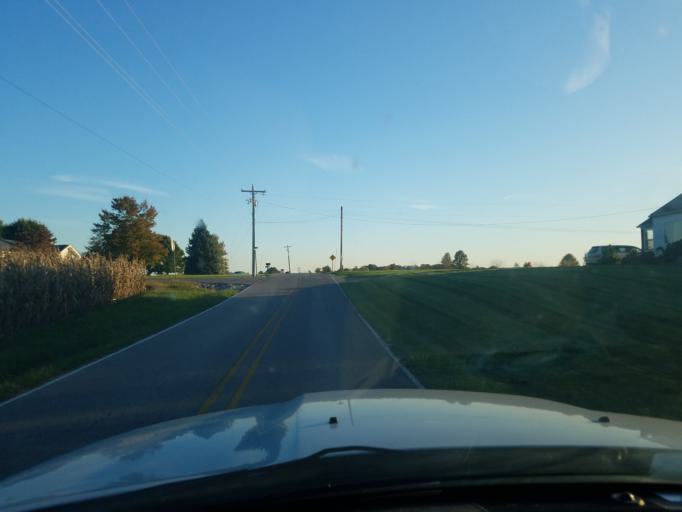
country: US
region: Indiana
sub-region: Floyd County
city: Galena
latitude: 38.4118
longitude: -85.9109
